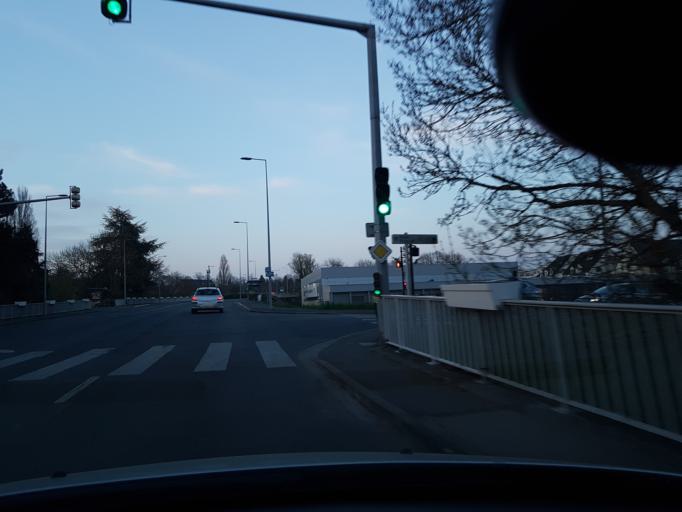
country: FR
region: Centre
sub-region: Departement du Cher
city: Bourges
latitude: 47.0912
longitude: 2.3988
